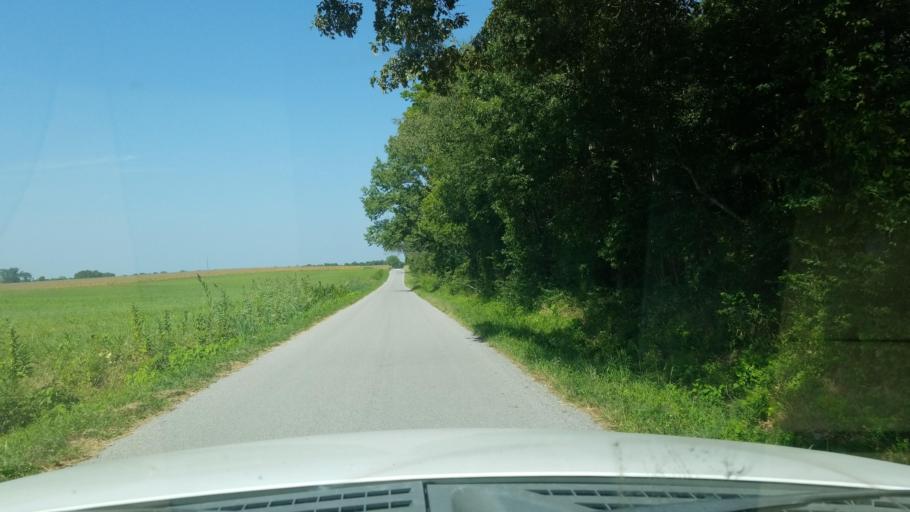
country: US
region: Illinois
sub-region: Saline County
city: Harrisburg
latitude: 37.8922
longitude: -88.6661
